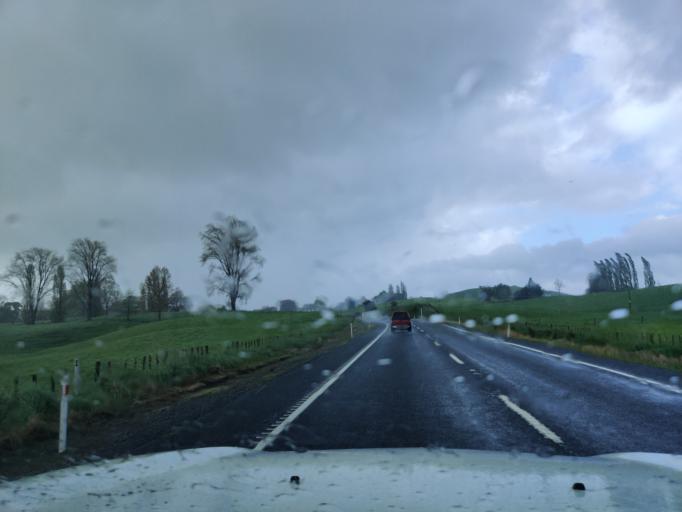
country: NZ
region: Waikato
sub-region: Matamata-Piako District
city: Matamata
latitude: -37.9810
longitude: 175.7032
